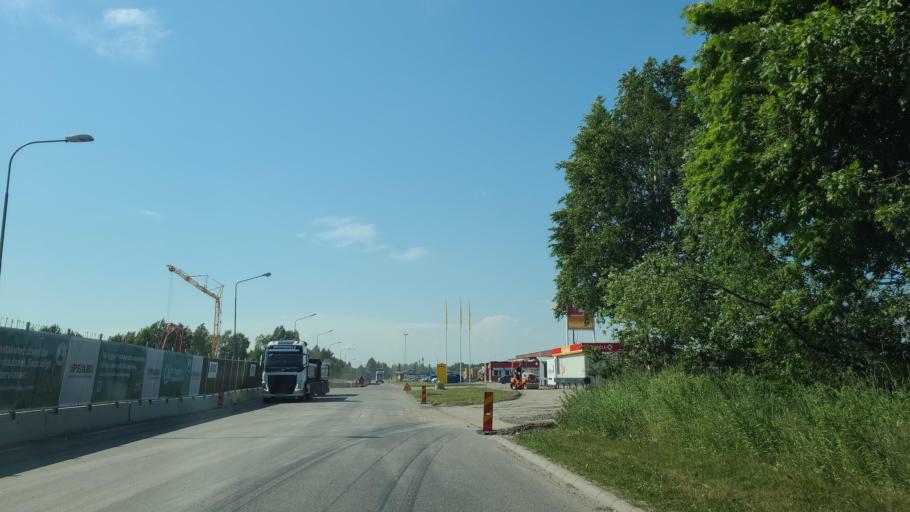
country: SE
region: Vaesterbotten
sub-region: Umea Kommun
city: Umea
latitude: 63.8428
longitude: 20.2211
